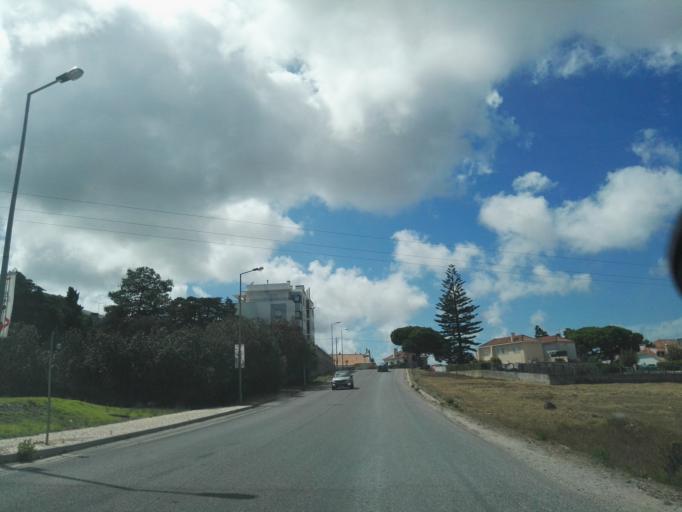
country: PT
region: Setubal
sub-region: Sesimbra
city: Sesimbra
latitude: 38.4656
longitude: -9.0980
